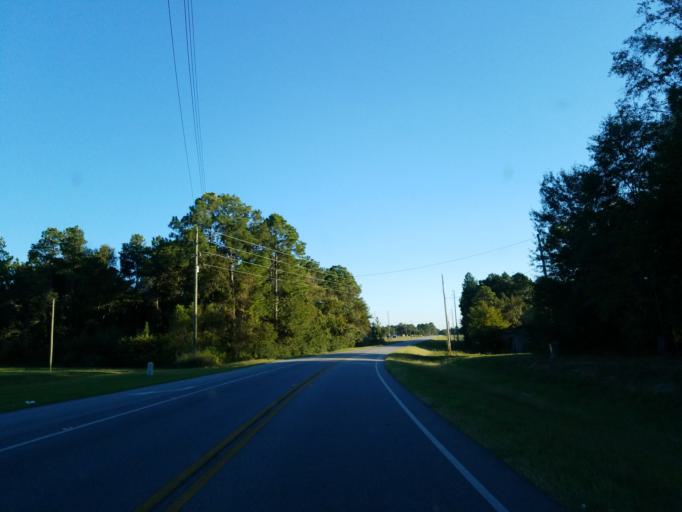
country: US
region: Georgia
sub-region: Worth County
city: Sylvester
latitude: 31.5532
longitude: -83.8432
